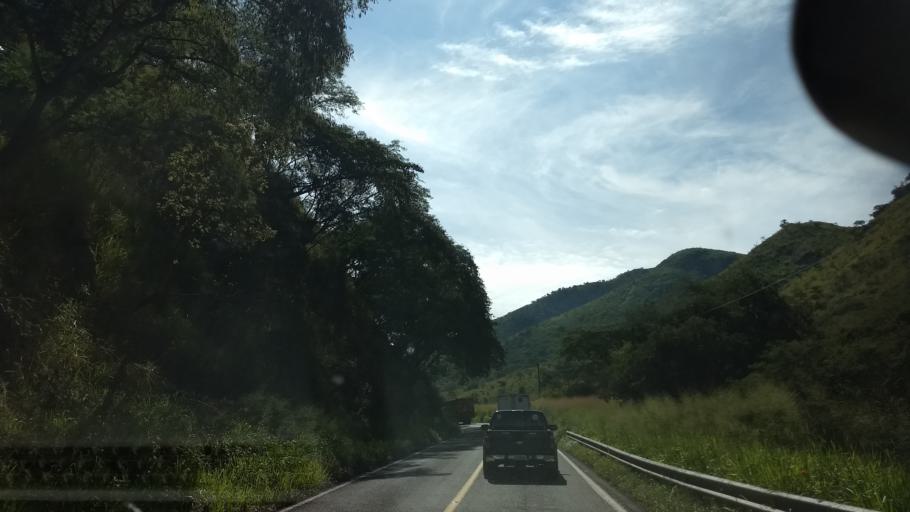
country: MX
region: Jalisco
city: Tuxpan
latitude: 19.5249
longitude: -103.4282
